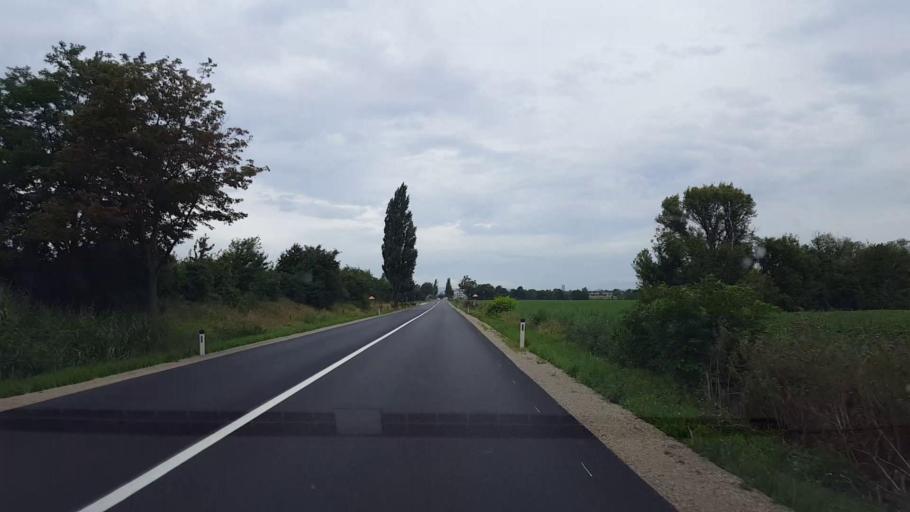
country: AT
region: Lower Austria
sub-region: Politischer Bezirk Wien-Umgebung
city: Schwechat
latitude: 48.1285
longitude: 16.5020
